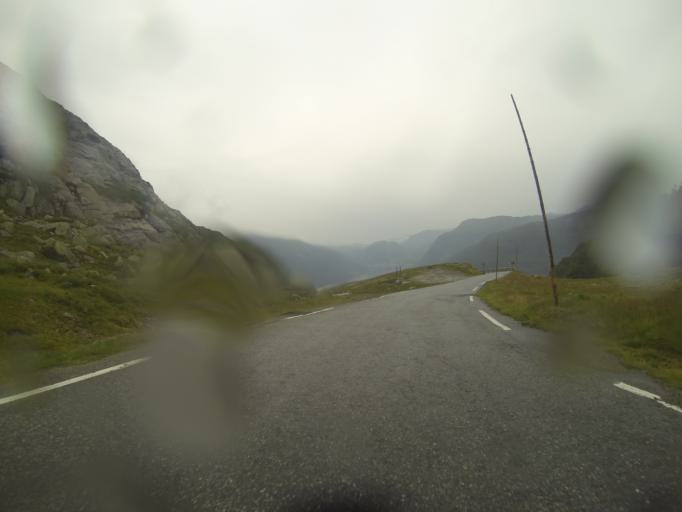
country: NO
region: Hordaland
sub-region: Odda
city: Odda
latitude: 59.7815
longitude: 6.7533
